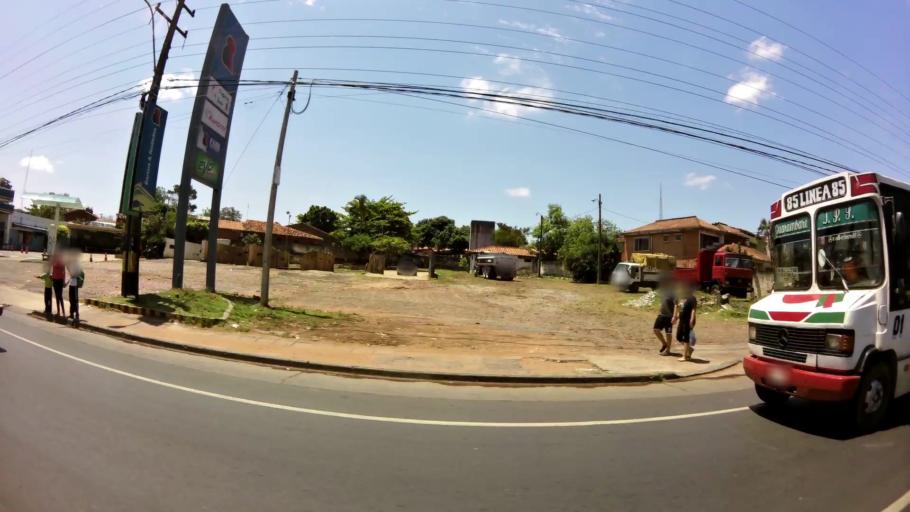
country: PY
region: Central
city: Villa Elisa
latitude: -25.3686
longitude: -57.5613
